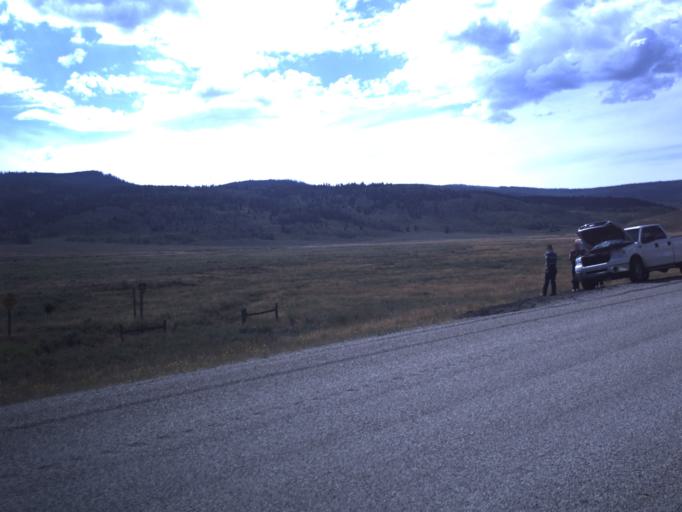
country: US
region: Utah
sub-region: Wasatch County
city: Heber
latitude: 40.2621
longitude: -111.2076
